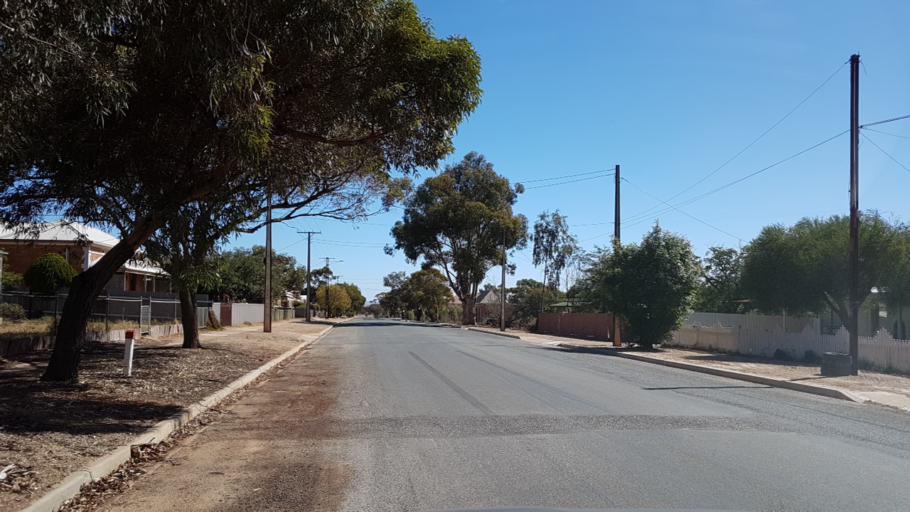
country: AU
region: South Australia
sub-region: Peterborough
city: Peterborough
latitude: -32.9786
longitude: 138.8302
